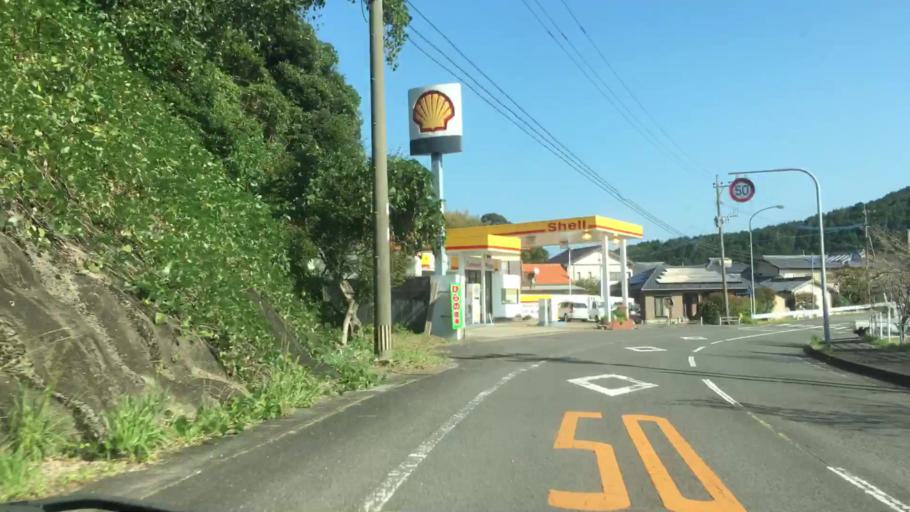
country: JP
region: Nagasaki
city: Sasebo
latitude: 32.9930
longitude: 129.6511
